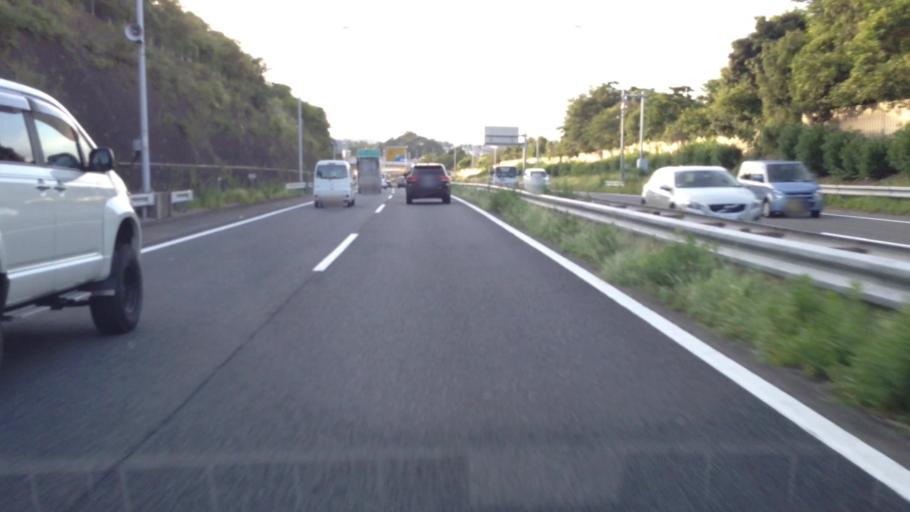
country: JP
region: Kanagawa
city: Kamakura
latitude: 35.3790
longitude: 139.5869
